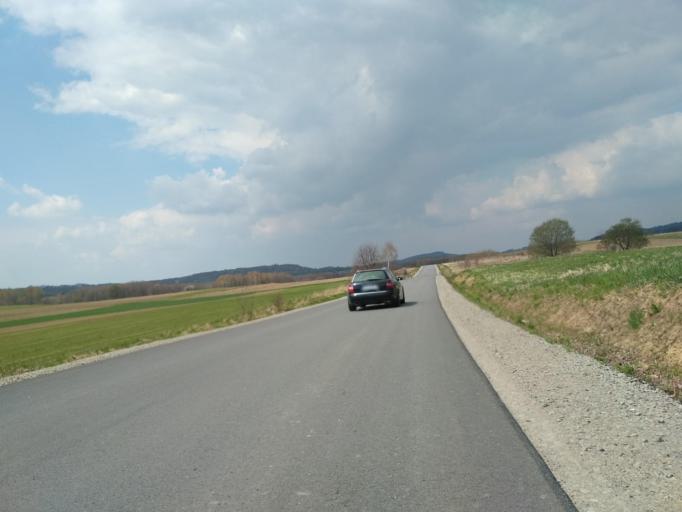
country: PL
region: Subcarpathian Voivodeship
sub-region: Powiat sanocki
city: Strachocina
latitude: 49.5894
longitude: 22.1081
